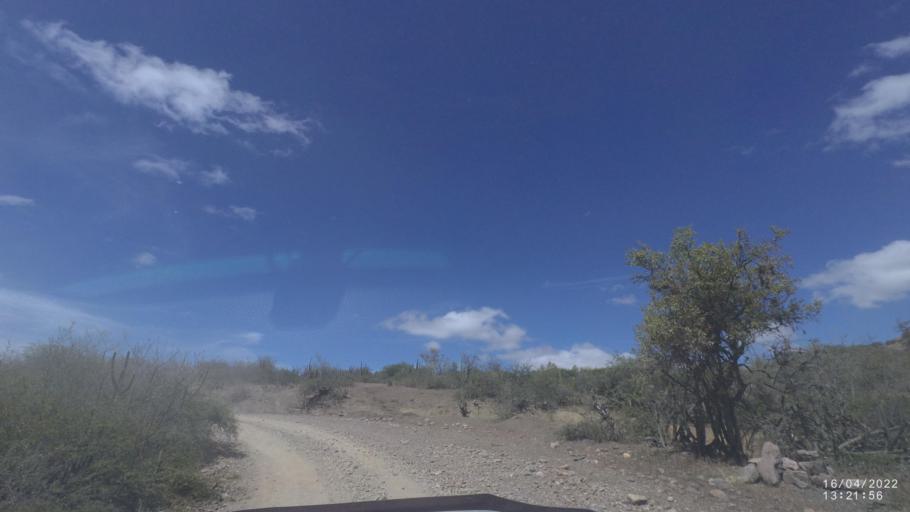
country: BO
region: Cochabamba
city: Mizque
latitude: -17.9921
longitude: -65.6088
